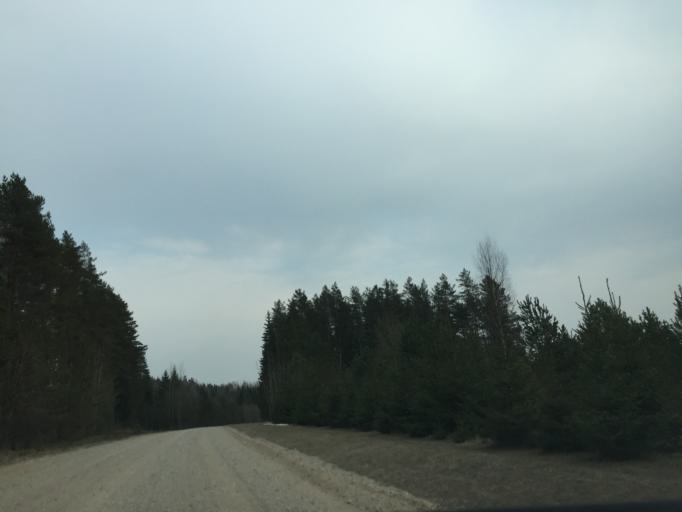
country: LV
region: Raunas
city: Rauna
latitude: 57.1637
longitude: 25.5183
